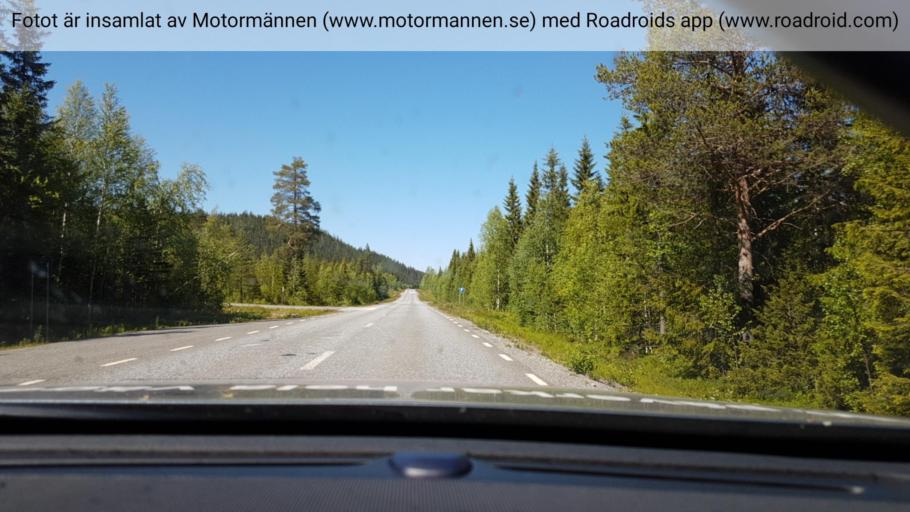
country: SE
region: Vaesterbotten
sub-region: Vilhelmina Kommun
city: Sjoberg
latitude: 64.8743
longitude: 15.8816
